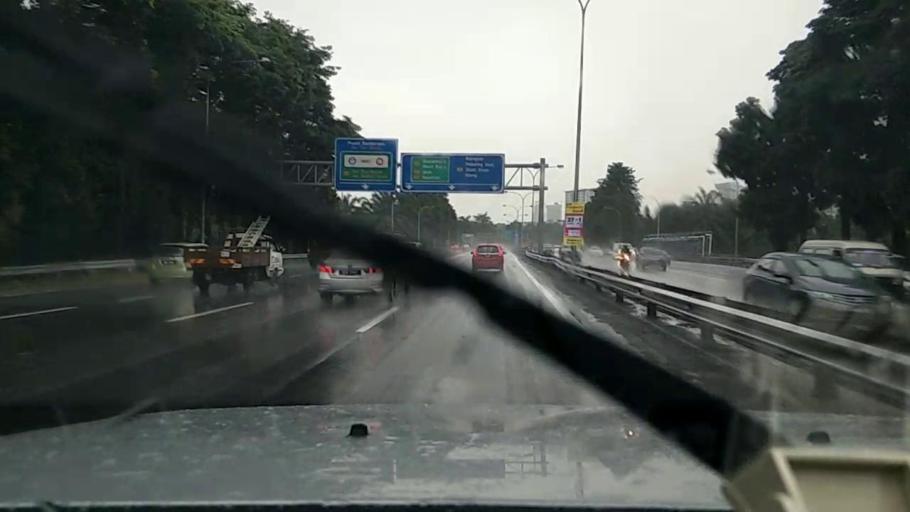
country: MY
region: Kuala Lumpur
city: Kuala Lumpur
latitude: 3.1009
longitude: 101.6979
